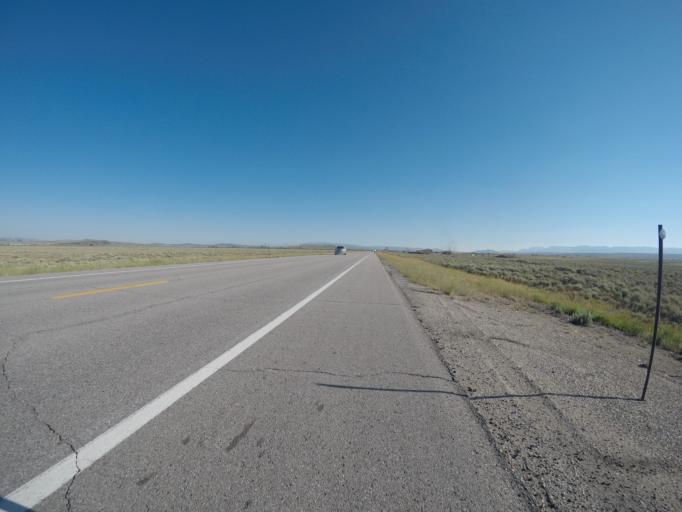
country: US
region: Wyoming
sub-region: Sublette County
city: Pinedale
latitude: 42.9643
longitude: -110.0885
